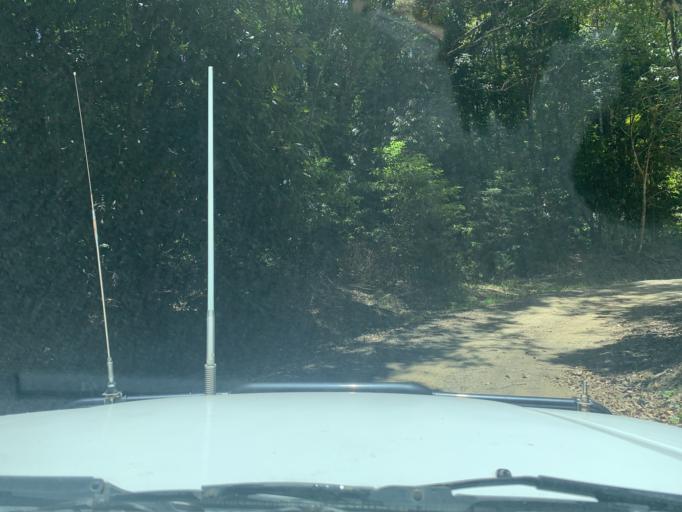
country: AU
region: Queensland
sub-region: Cairns
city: Redlynch
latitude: -16.9654
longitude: 145.6462
